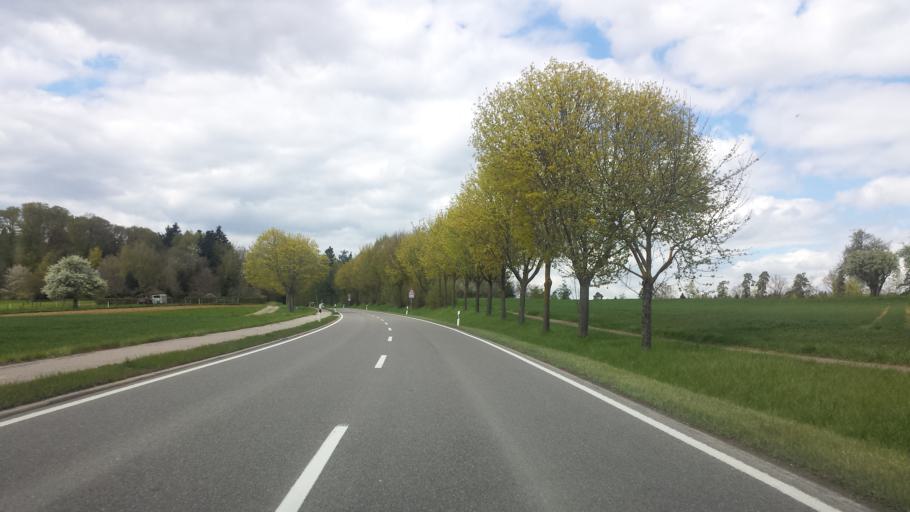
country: DE
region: Baden-Wuerttemberg
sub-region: Regierungsbezirk Stuttgart
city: Rutesheim
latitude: 48.8184
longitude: 8.9365
